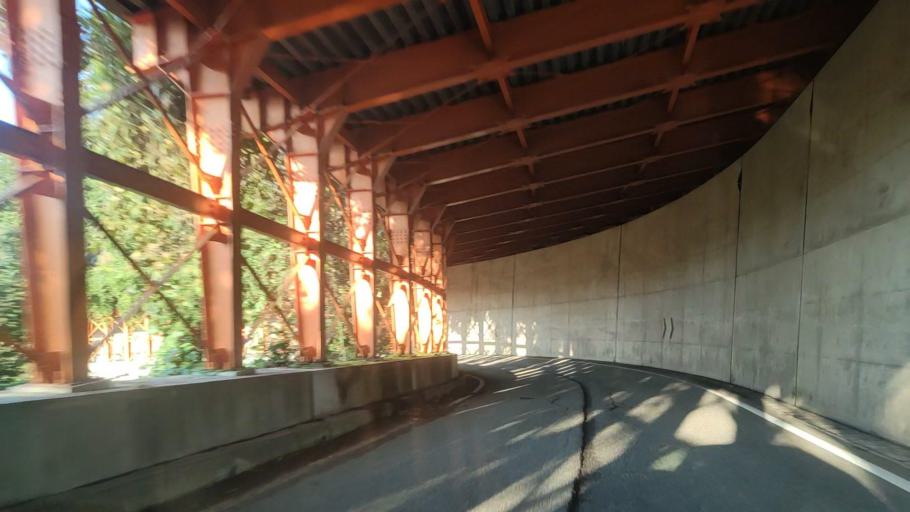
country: JP
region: Toyama
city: Yatsuomachi-higashikumisaka
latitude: 36.5075
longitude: 137.0223
